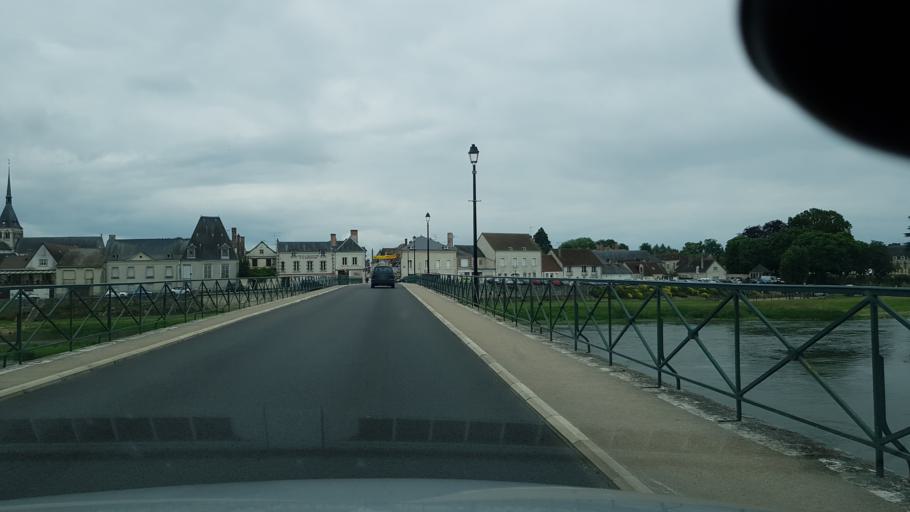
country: FR
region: Centre
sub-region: Departement du Loir-et-Cher
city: Selles-sur-Cher
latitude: 47.2776
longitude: 1.5507
